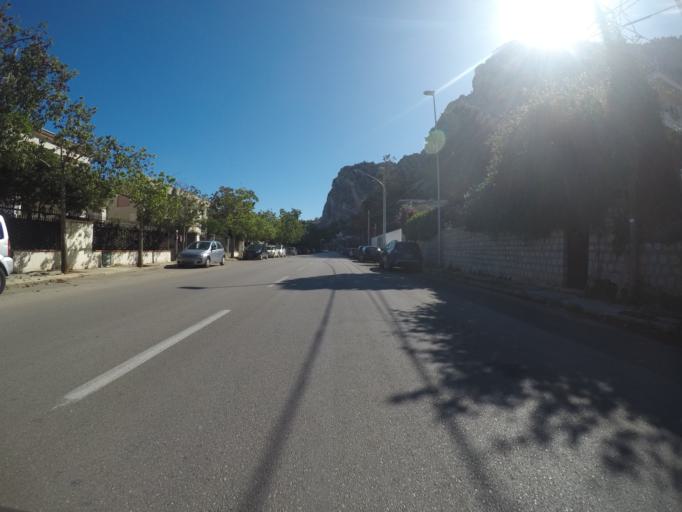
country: IT
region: Sicily
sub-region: Palermo
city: Palermo
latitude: 38.1888
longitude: 13.3495
